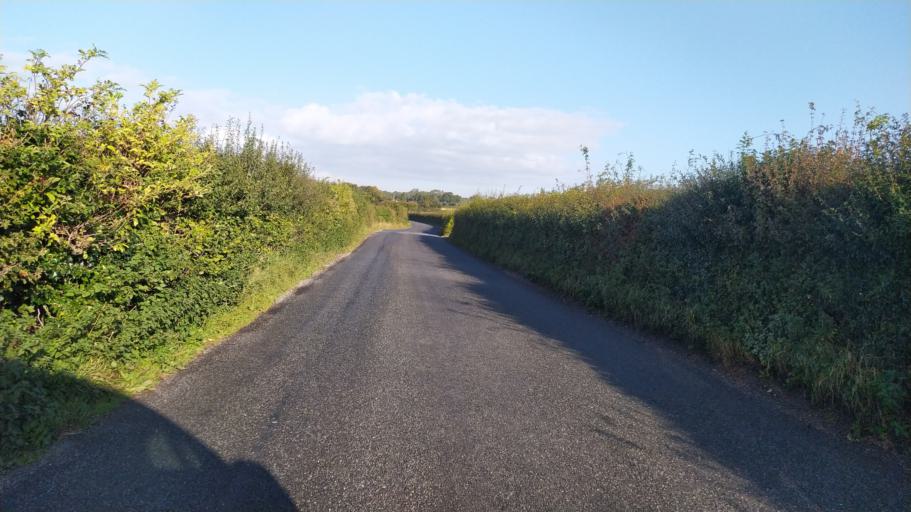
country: GB
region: England
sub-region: Wiltshire
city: Ansty
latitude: 50.9349
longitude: -2.0679
